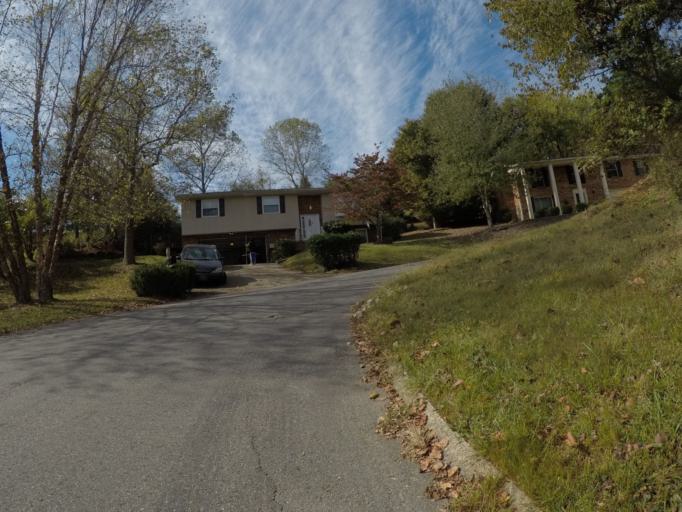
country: US
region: West Virginia
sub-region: Cabell County
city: Huntington
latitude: 38.3931
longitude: -82.3938
